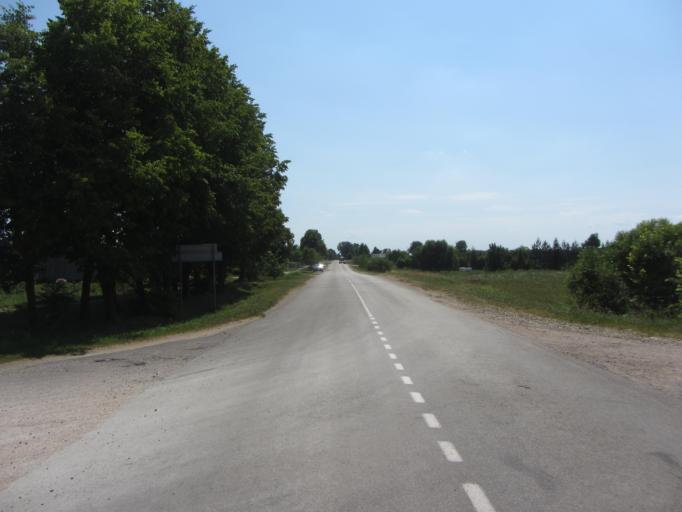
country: LT
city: Sirvintos
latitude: 55.1271
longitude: 24.9787
